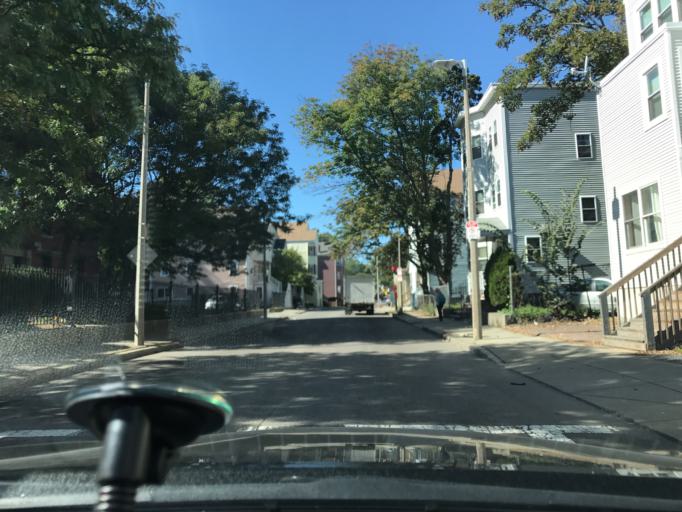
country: US
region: Massachusetts
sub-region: Suffolk County
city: South Boston
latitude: 42.3134
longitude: -71.0761
